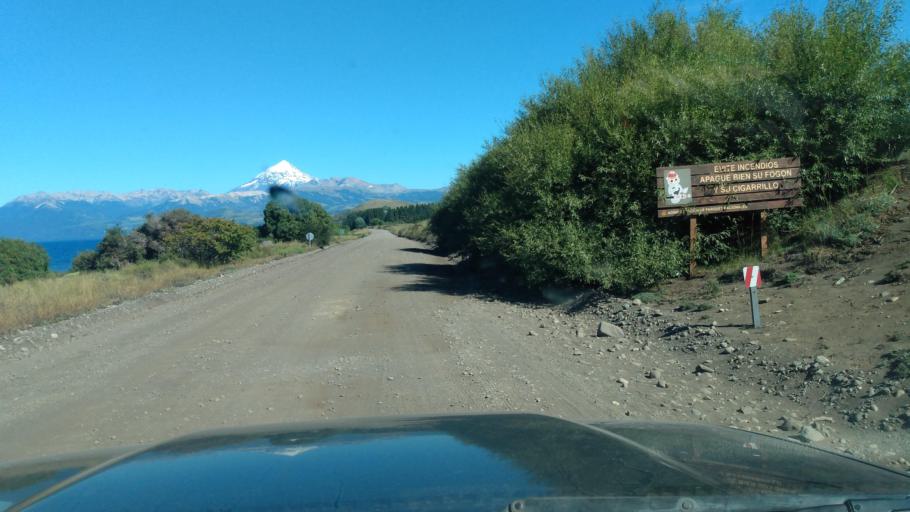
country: AR
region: Neuquen
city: Junin de los Andes
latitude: -39.7898
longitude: -71.2184
